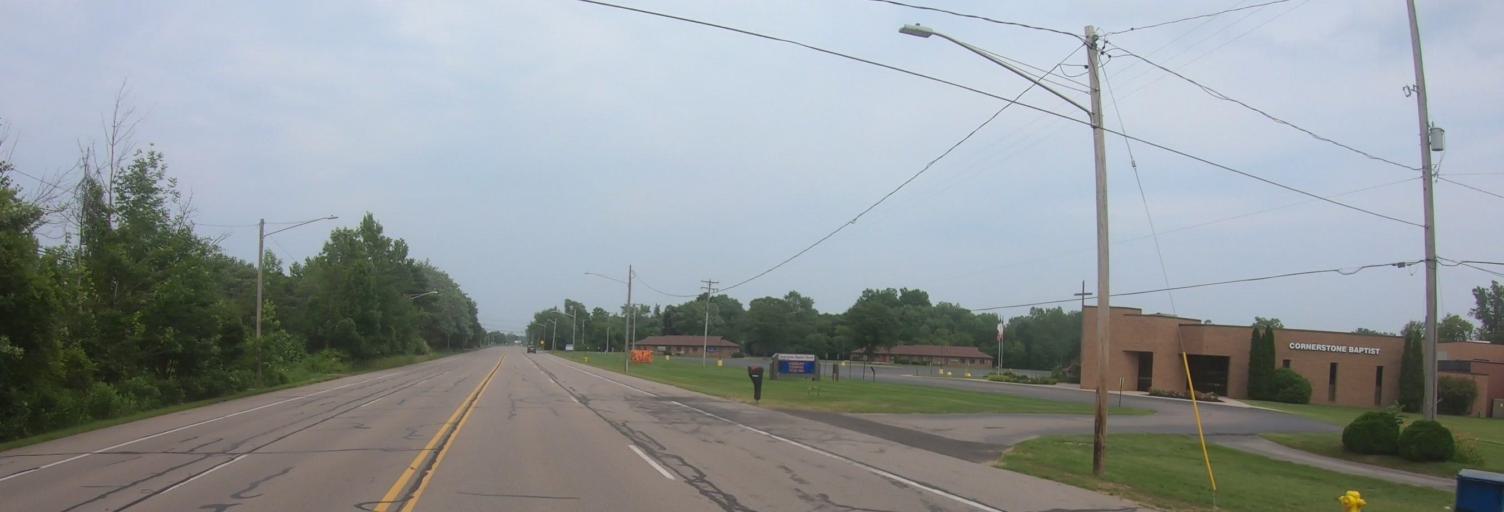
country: US
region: Michigan
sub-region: Genesee County
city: Swartz Creek
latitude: 42.9690
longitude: -83.8012
